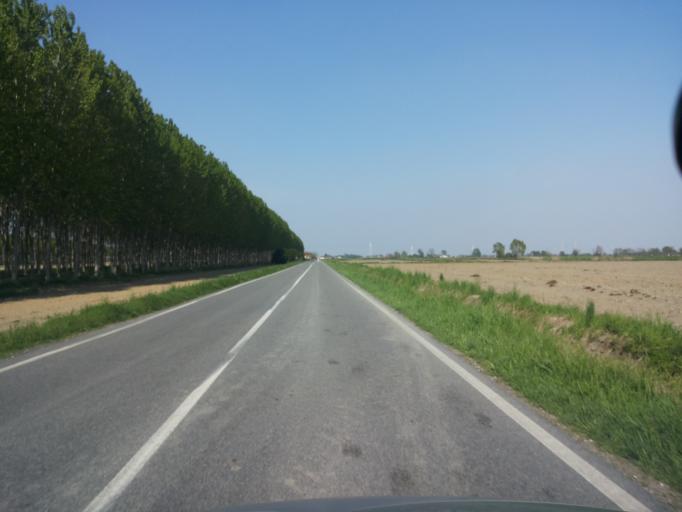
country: IT
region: Lombardy
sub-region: Provincia di Pavia
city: Zeme
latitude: 45.2151
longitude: 8.6545
